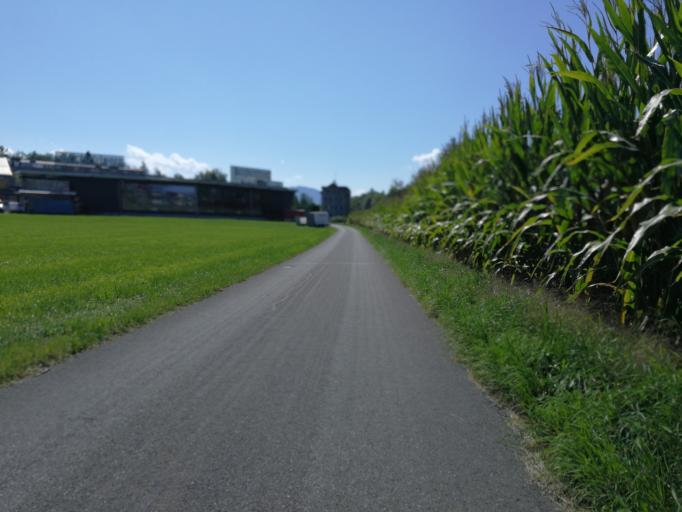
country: CH
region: Zurich
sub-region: Bezirk Hinwil
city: Rueti / Westlicher Dorfteil
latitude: 47.2647
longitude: 8.8347
